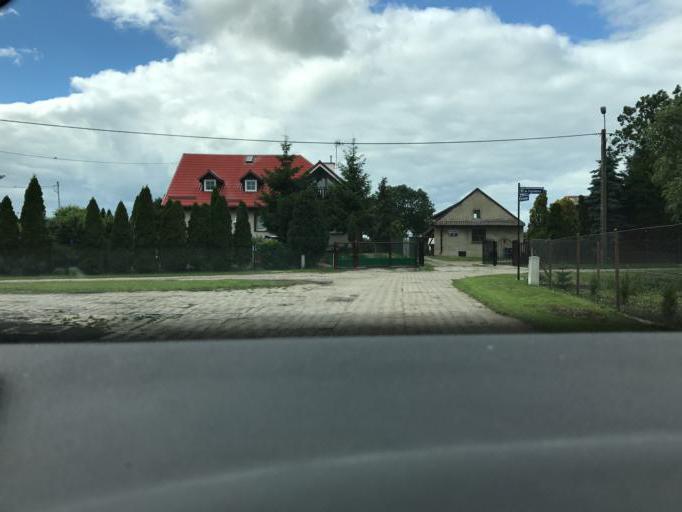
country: PL
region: Pomeranian Voivodeship
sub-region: Powiat gdanski
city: Pruszcz Gdanski
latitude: 54.2754
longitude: 18.6921
